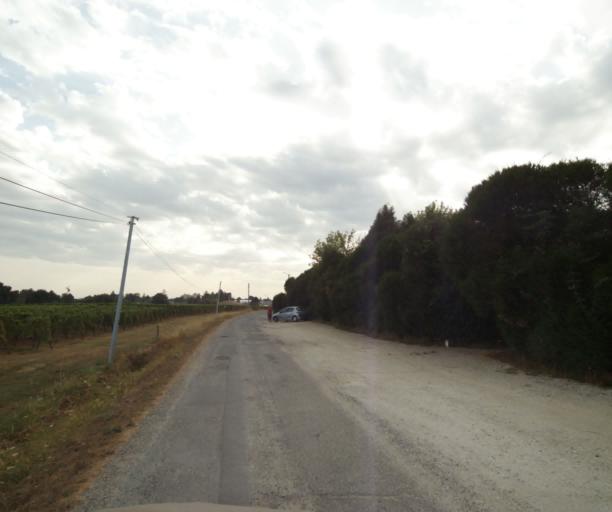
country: FR
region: Aquitaine
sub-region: Departement de la Gironde
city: Creon
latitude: 44.7720
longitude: -0.3598
